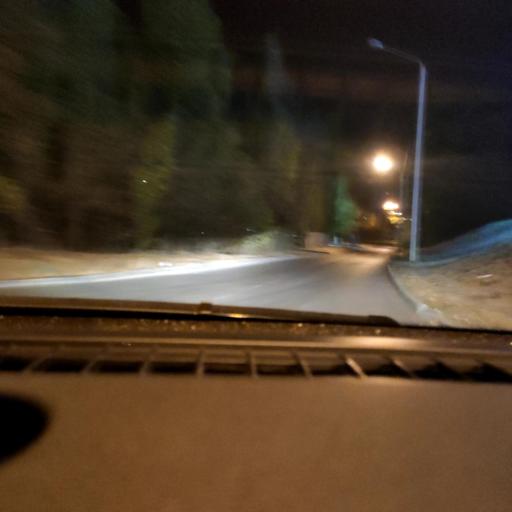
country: RU
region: Voronezj
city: Voronezh
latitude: 51.6618
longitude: 39.1323
